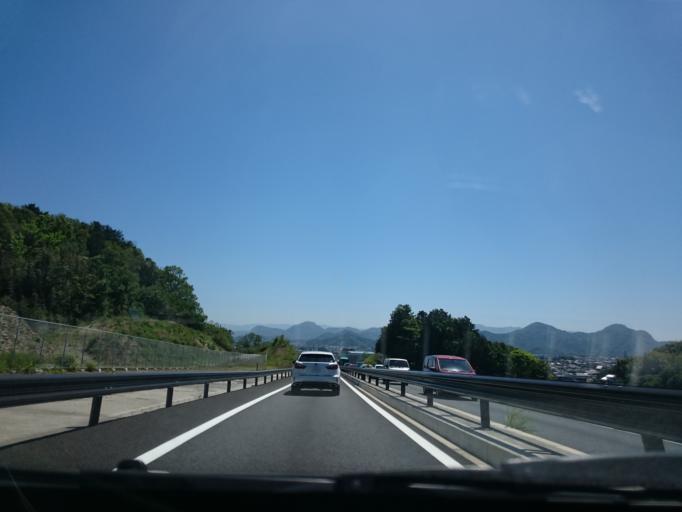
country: JP
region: Shizuoka
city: Mishima
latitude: 35.1020
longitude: 138.9485
